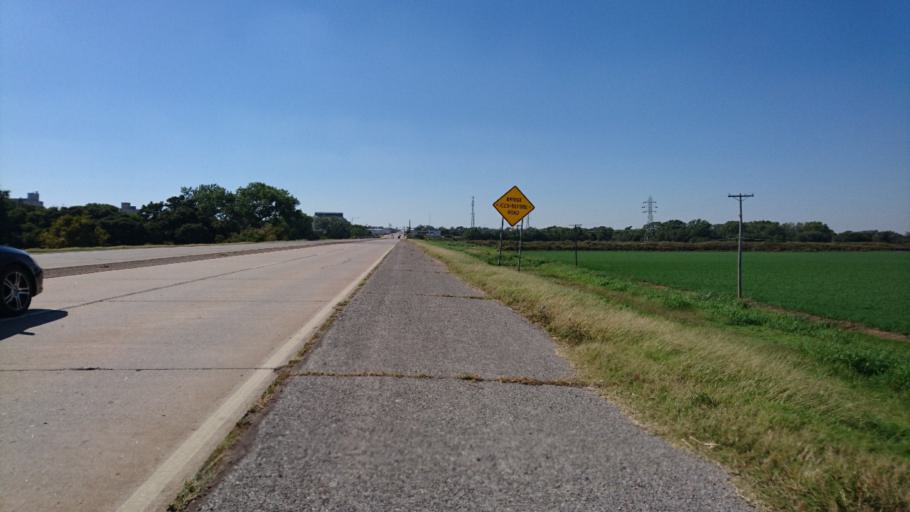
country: US
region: Oklahoma
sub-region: Custer County
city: Clinton
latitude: 35.5157
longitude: -98.9524
